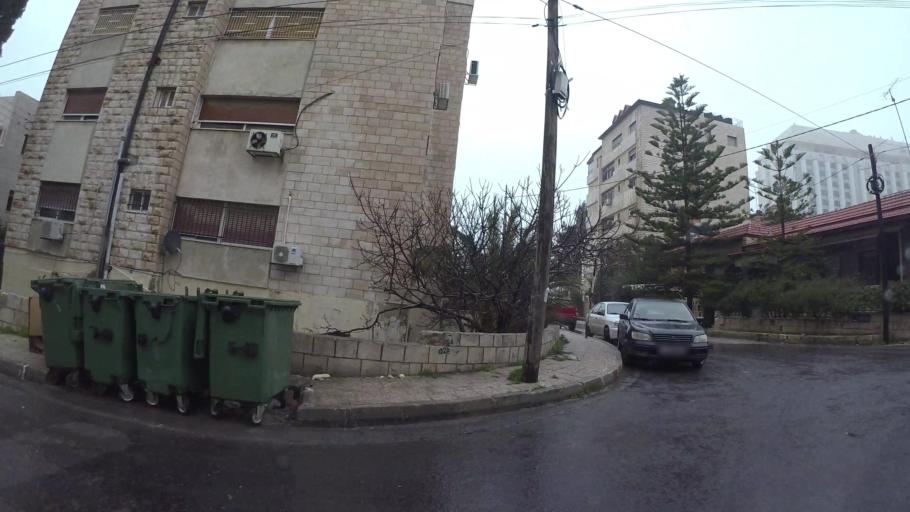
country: JO
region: Amman
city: Wadi as Sir
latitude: 31.9635
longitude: 35.8813
